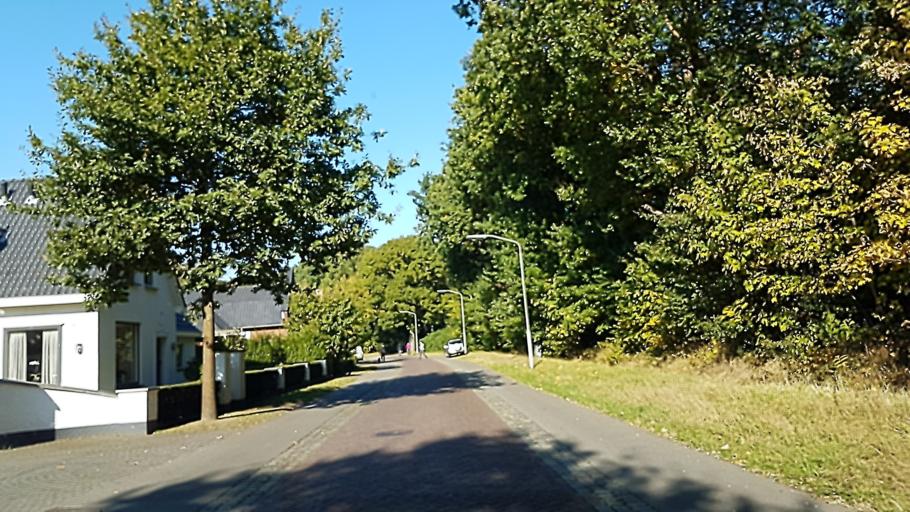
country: NL
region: North Brabant
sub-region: Gemeente Woensdrecht
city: Woensdrecht
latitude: 51.4380
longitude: 4.3182
